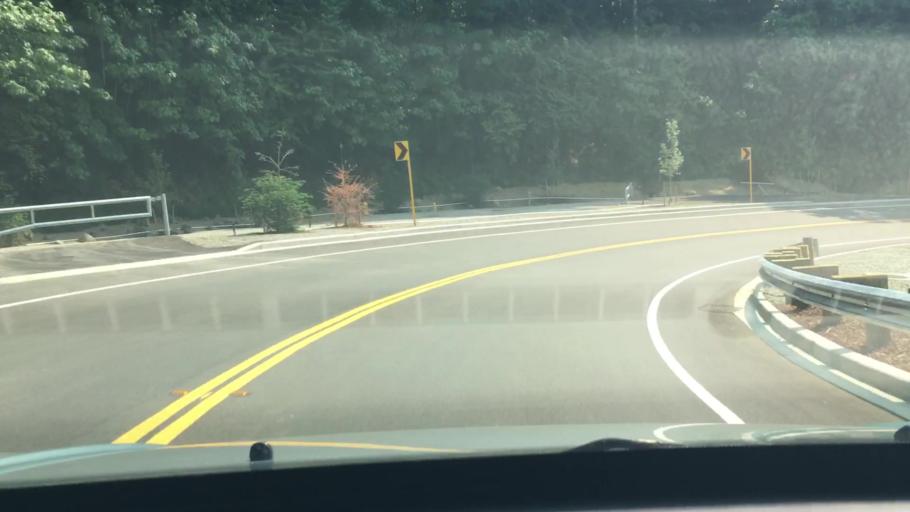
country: US
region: Washington
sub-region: King County
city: City of Sammamish
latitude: 47.5735
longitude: -122.0586
